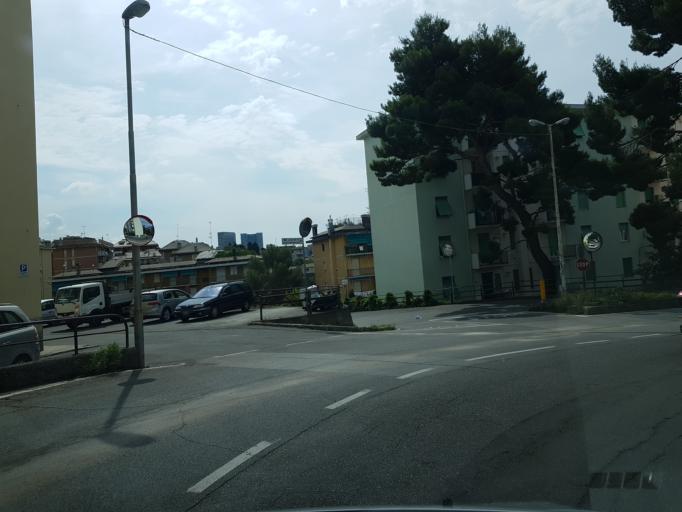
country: IT
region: Liguria
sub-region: Provincia di Genova
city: San Teodoro
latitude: 44.4317
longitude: 8.8456
